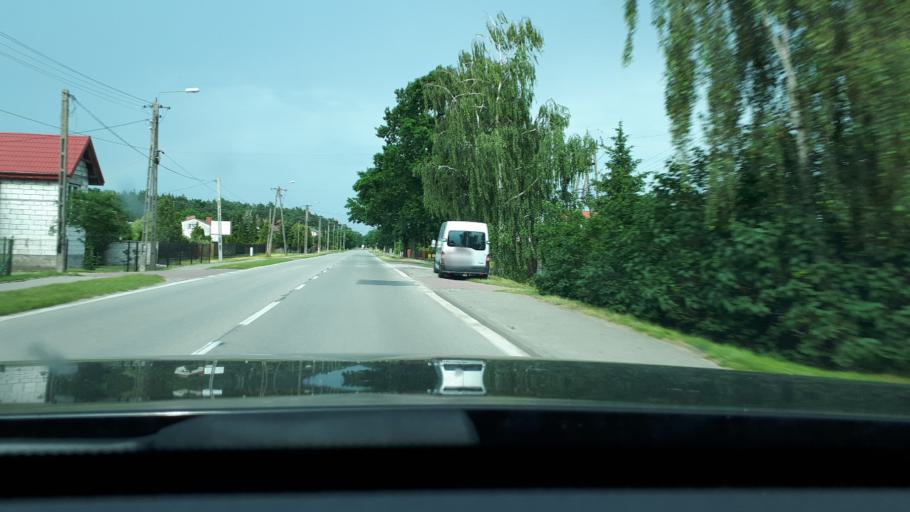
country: PL
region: Masovian Voivodeship
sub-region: Powiat warszawski zachodni
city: Leszno
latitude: 52.2620
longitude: 20.6302
